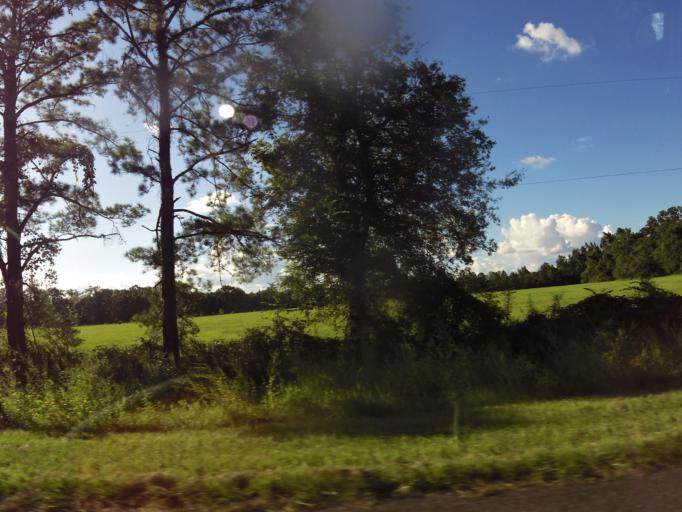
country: US
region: Florida
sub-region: Wakulla County
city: Crawfordville
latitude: 30.0650
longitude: -84.5162
